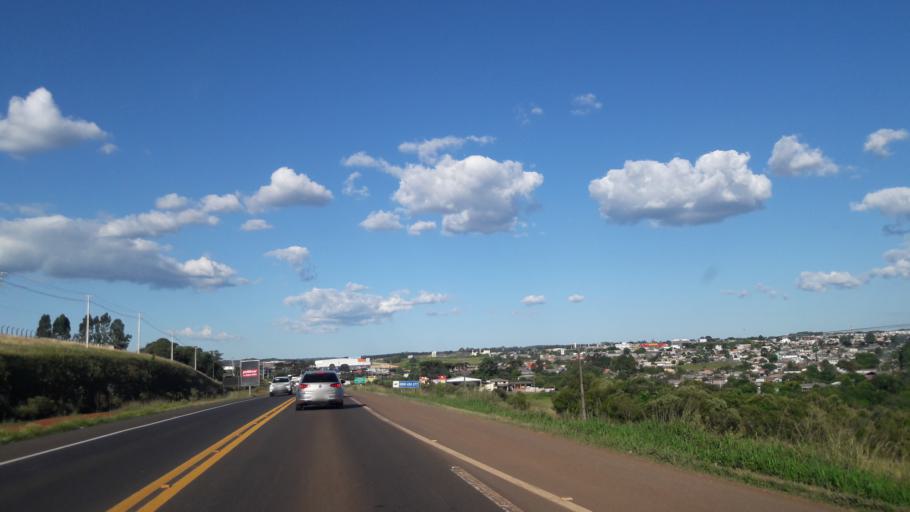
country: BR
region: Parana
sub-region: Guarapuava
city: Guarapuava
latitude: -25.3702
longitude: -51.4973
